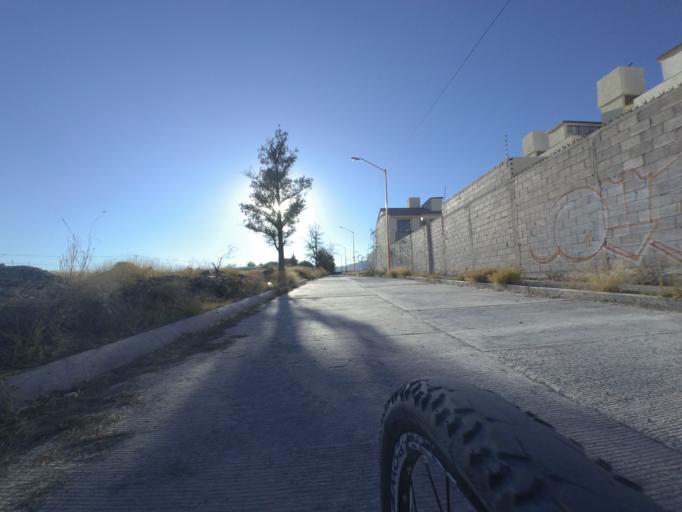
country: MX
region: Aguascalientes
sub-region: Aguascalientes
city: La Loma de los Negritos
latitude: 21.8505
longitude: -102.3449
